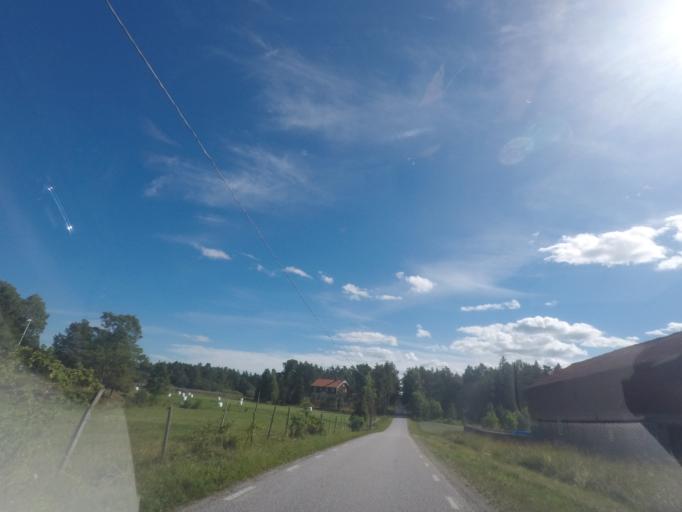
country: SE
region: Stockholm
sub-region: Norrtalje Kommun
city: Arno
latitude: 60.1932
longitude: 18.7425
